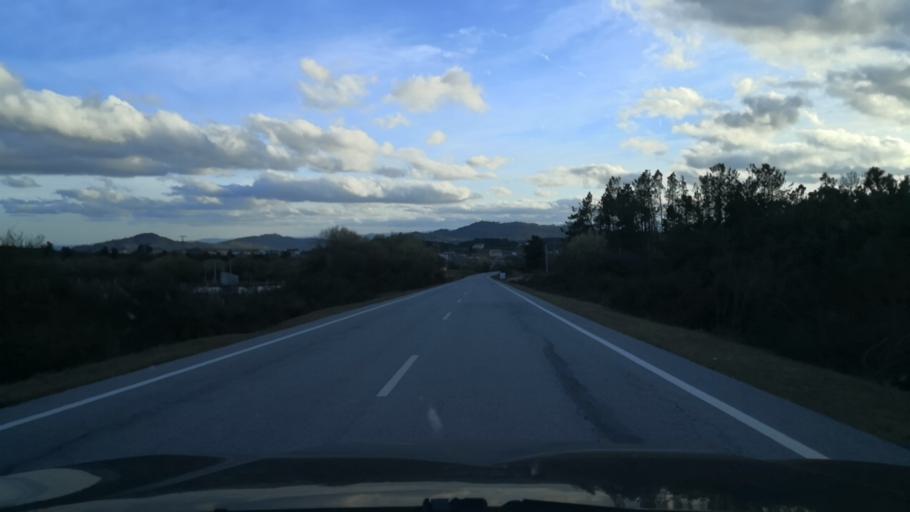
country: PT
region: Braganca
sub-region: Carrazeda de Ansiaes
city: Carrazeda de Anciaes
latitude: 41.2441
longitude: -7.3186
